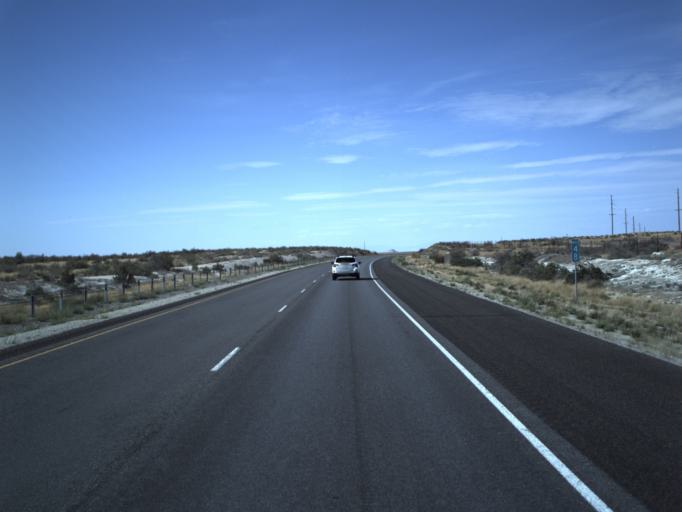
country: US
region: Utah
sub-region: Tooele County
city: Grantsville
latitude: 40.7278
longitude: -113.1306
